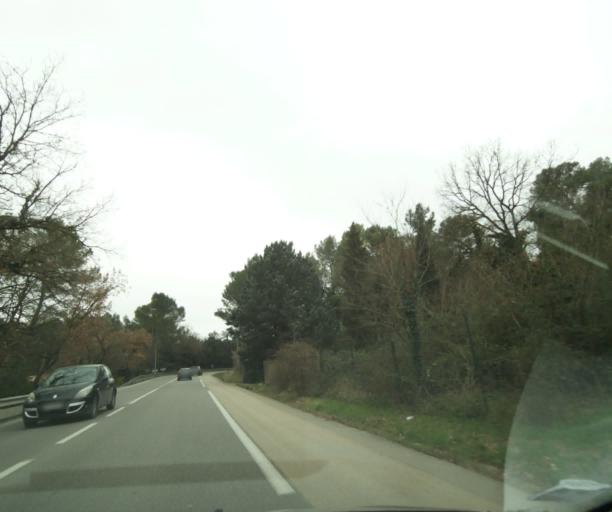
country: FR
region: Provence-Alpes-Cote d'Azur
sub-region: Departement des Bouches-du-Rhone
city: Fuveau
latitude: 43.4618
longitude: 5.5469
